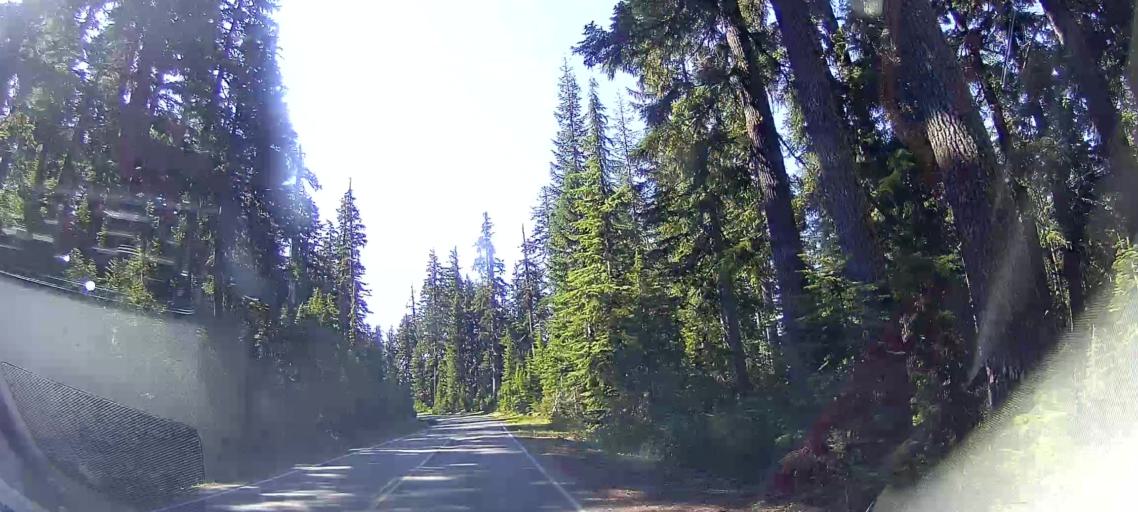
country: US
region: Oregon
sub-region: Jackson County
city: Shady Cove
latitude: 42.8830
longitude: -122.1291
